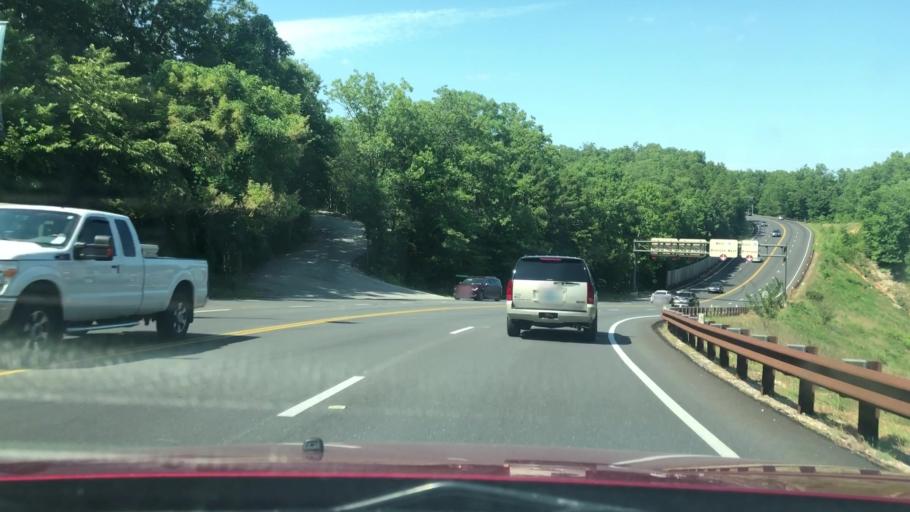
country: US
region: Missouri
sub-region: Stone County
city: Kimberling City
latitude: 36.6669
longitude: -93.3371
